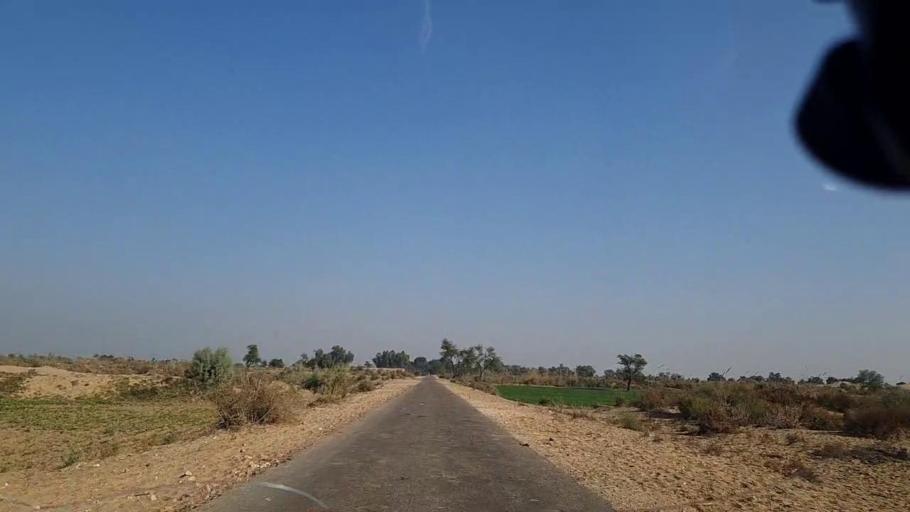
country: PK
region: Sindh
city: Khanpur
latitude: 27.6863
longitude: 69.4808
